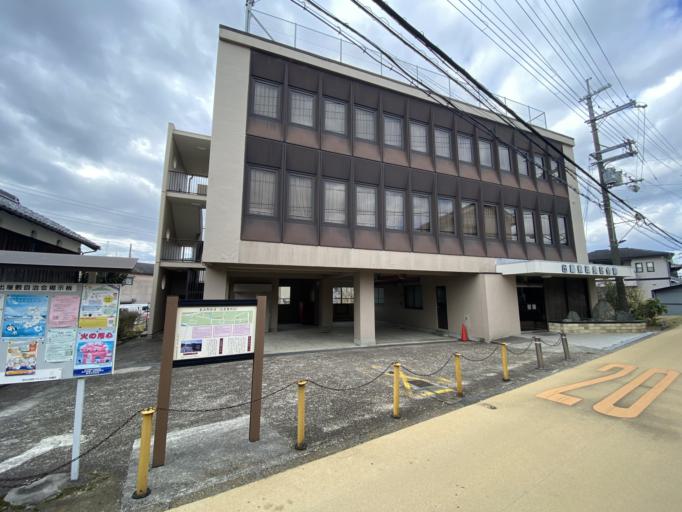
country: JP
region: Osaka
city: Hirakata
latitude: 34.8260
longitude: 135.6855
